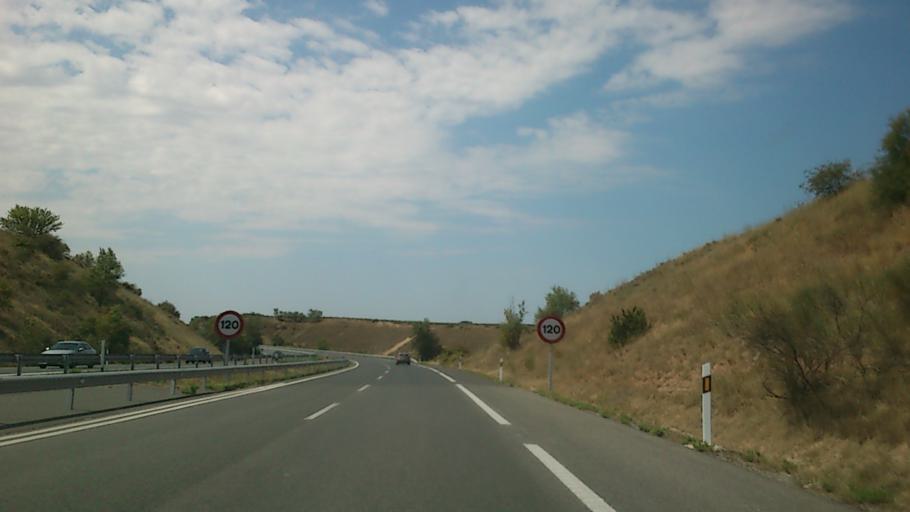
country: ES
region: La Rioja
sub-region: Provincia de La Rioja
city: Cenicero
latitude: 42.4761
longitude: -2.6514
